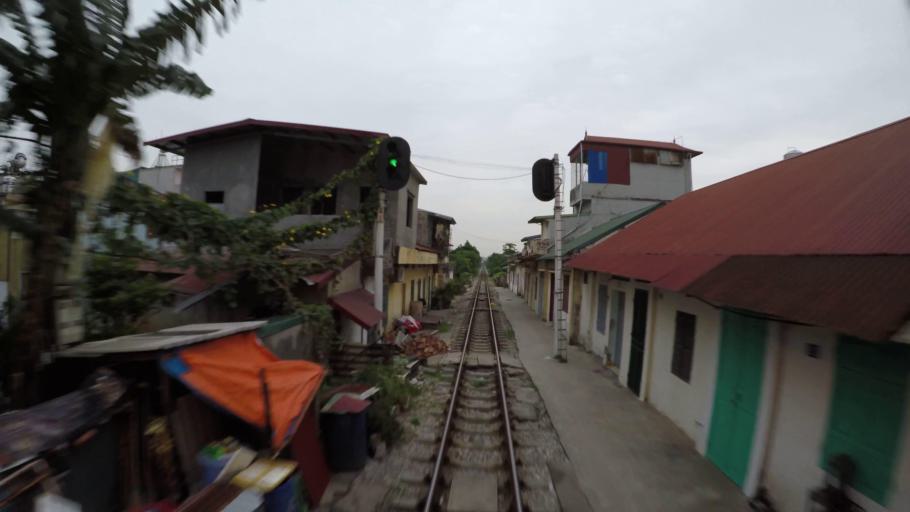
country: VN
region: Ha Noi
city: Hoan Kiem
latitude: 21.0475
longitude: 105.8932
